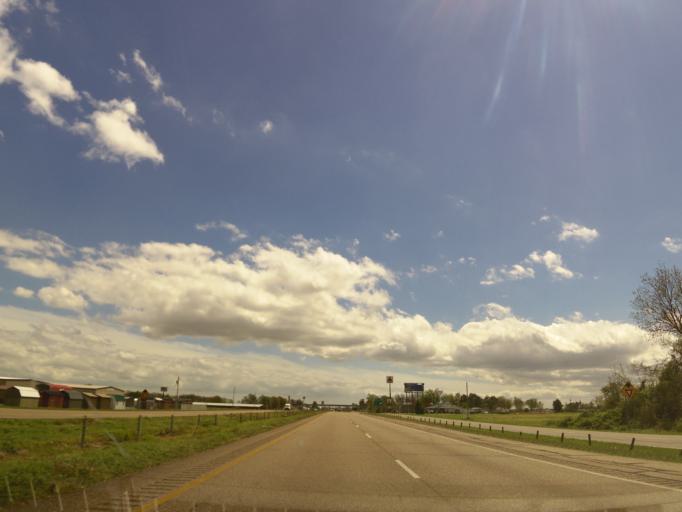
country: US
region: Arkansas
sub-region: Crittenden County
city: Marion
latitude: 35.2685
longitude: -90.2311
